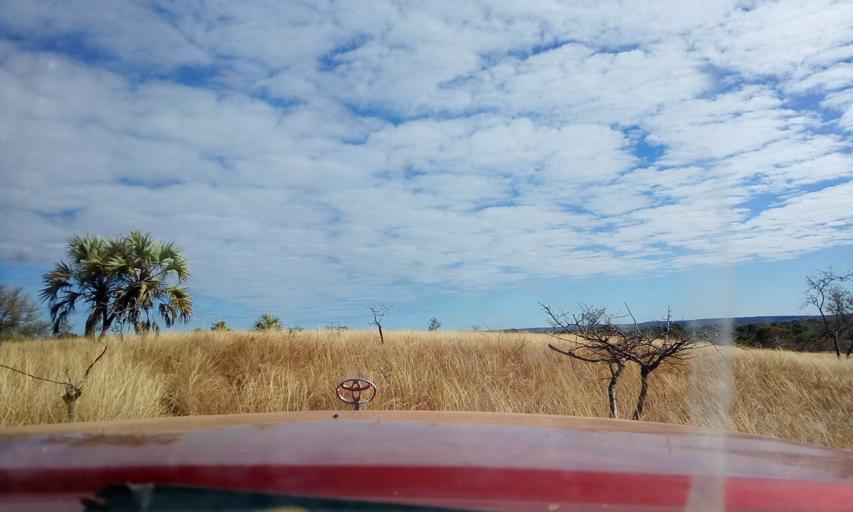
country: MG
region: Melaky
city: Mahabe
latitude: -16.3863
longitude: 45.3451
